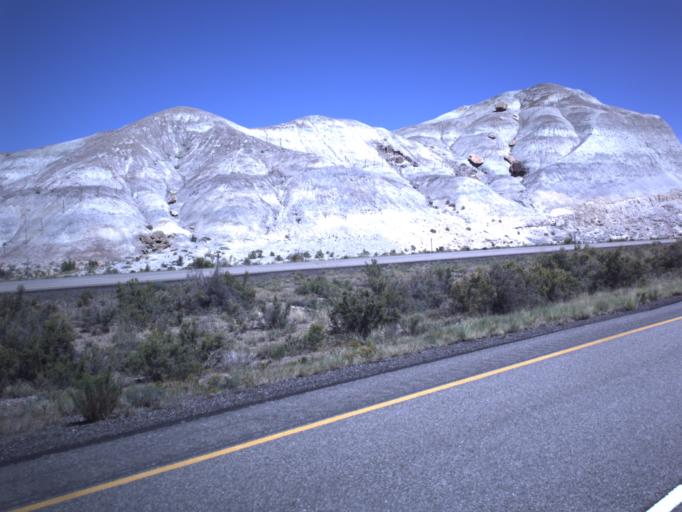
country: US
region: Utah
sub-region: Emery County
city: Ferron
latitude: 38.8168
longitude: -111.1761
